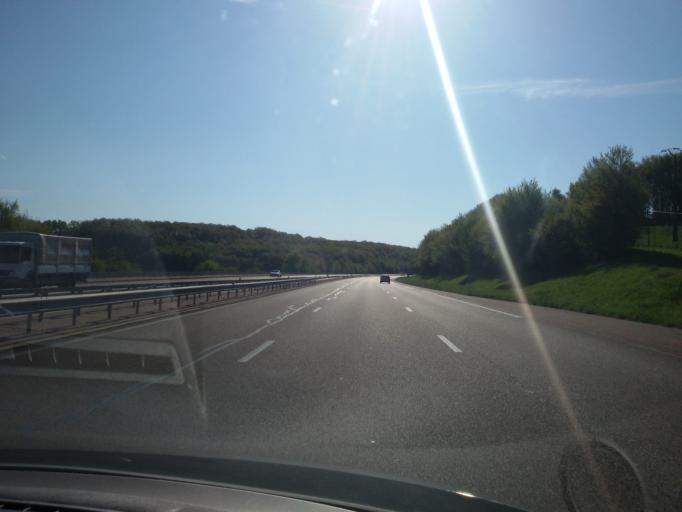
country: FR
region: Bourgogne
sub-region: Departement de l'Yonne
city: Cezy
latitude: 47.9277
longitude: 3.2653
